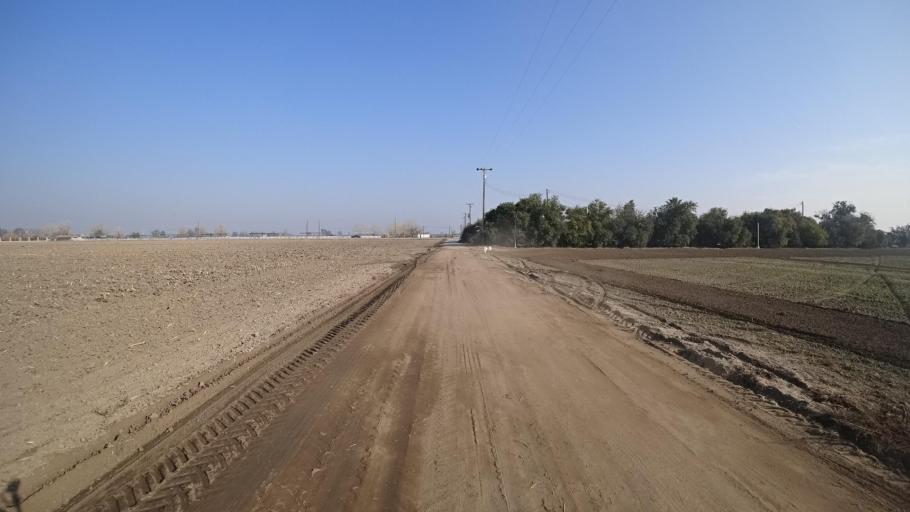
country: US
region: California
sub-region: Kern County
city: Greenfield
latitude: 35.2525
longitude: -119.0414
